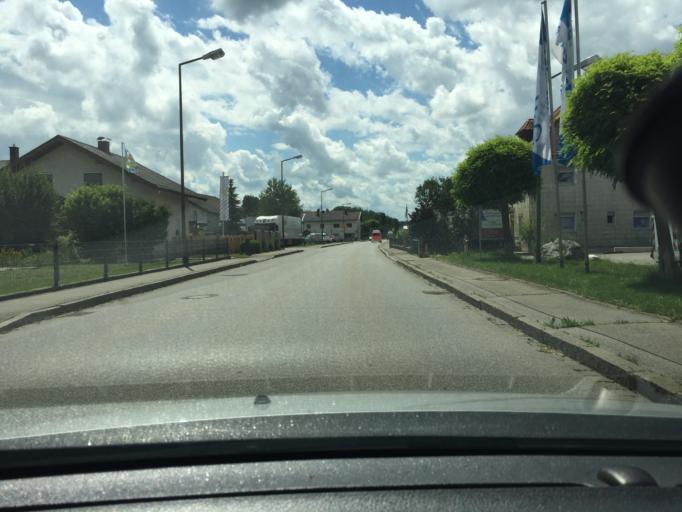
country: DE
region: Bavaria
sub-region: Upper Bavaria
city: Kienberg
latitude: 48.0697
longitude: 12.4888
